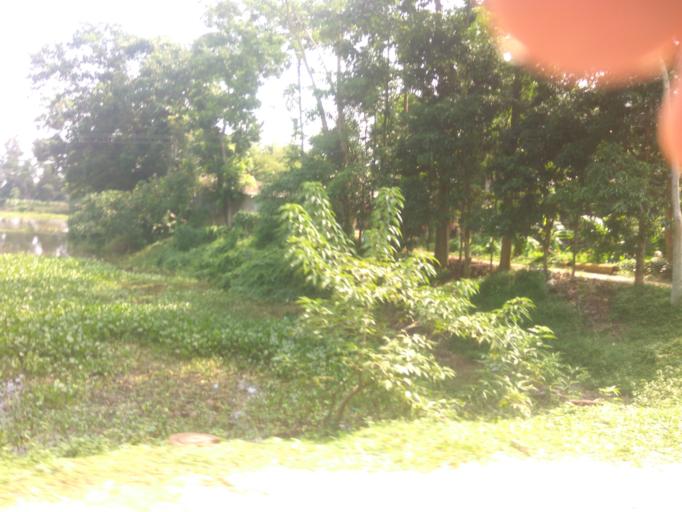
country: IN
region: Assam
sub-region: Karimganj
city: Karimganj
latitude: 24.8126
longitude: 92.1791
